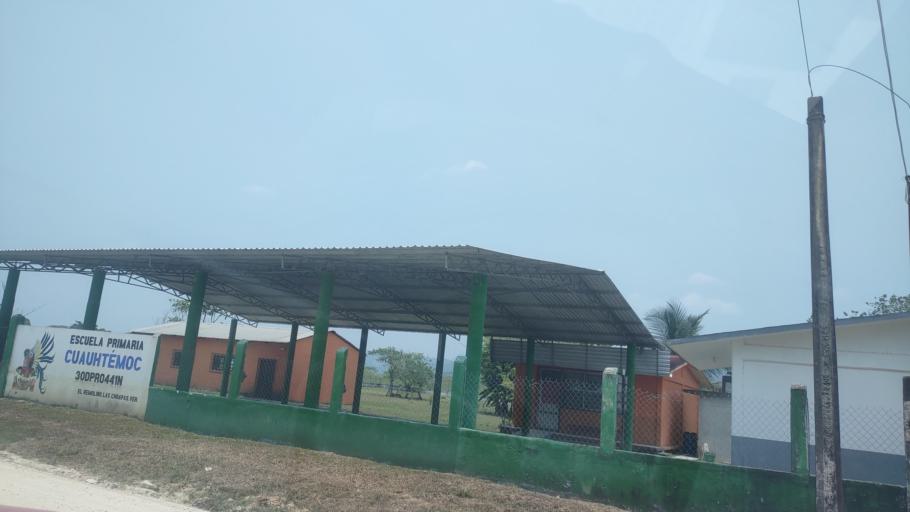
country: MX
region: Chiapas
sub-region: Tecpatan
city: Raudales Malpaso
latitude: 17.4593
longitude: -93.8021
